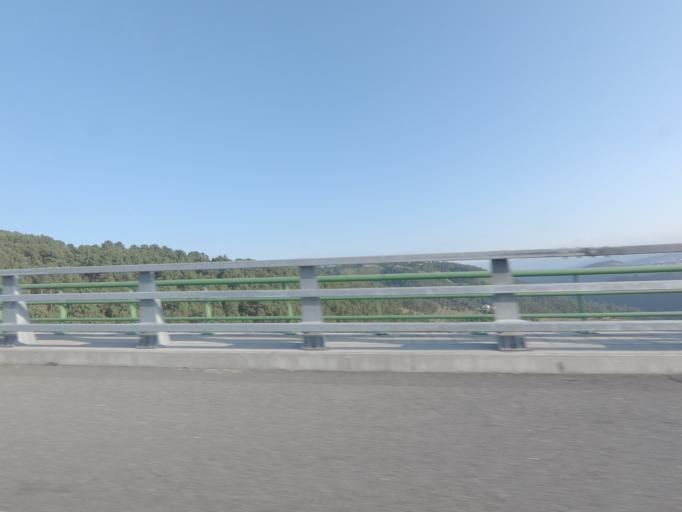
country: PT
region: Vila Real
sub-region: Vila Real
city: Vila Real
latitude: 41.2773
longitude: -7.7358
